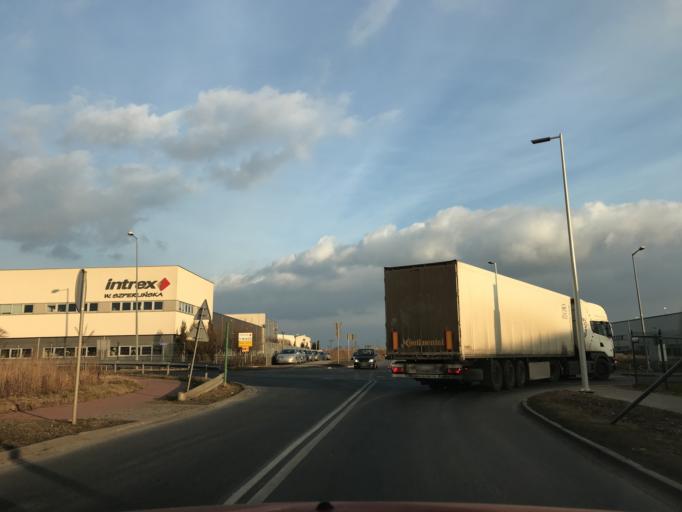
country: PL
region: Greater Poland Voivodeship
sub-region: Powiat poznanski
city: Baranowo
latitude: 52.4462
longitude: 16.7256
